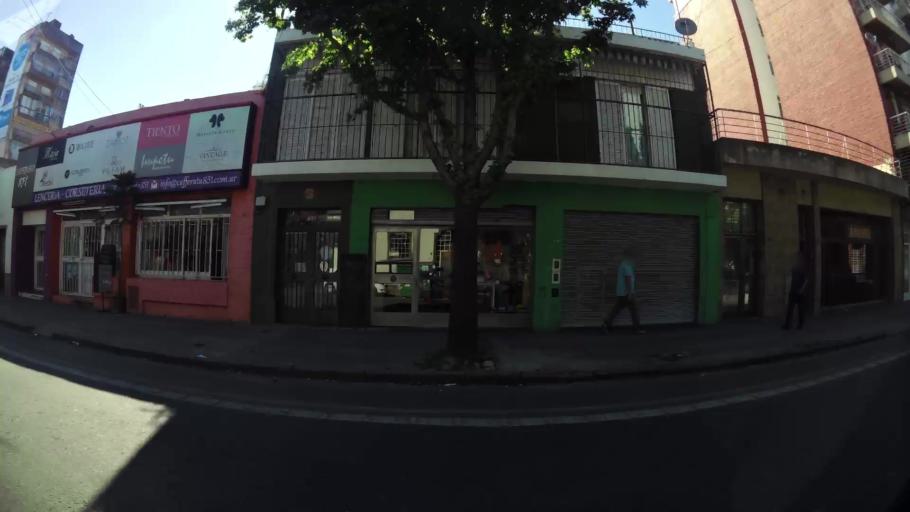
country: AR
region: Santa Fe
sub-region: Departamento de Rosario
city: Rosario
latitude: -32.9412
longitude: -60.6711
